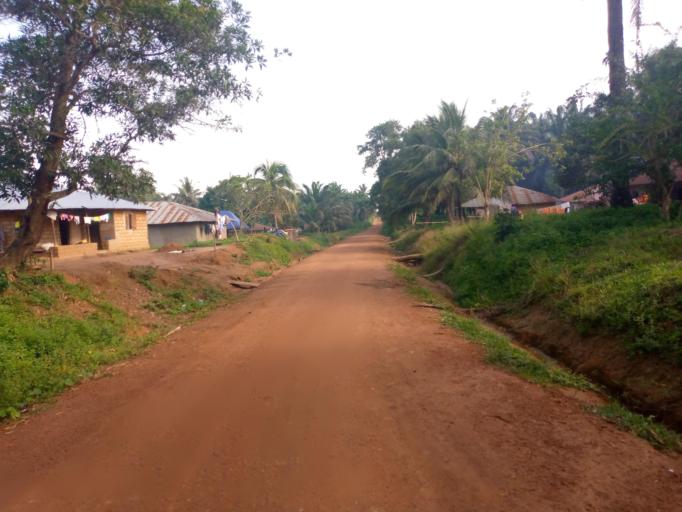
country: SL
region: Southern Province
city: Sumbuya
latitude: 7.6122
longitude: -12.1425
